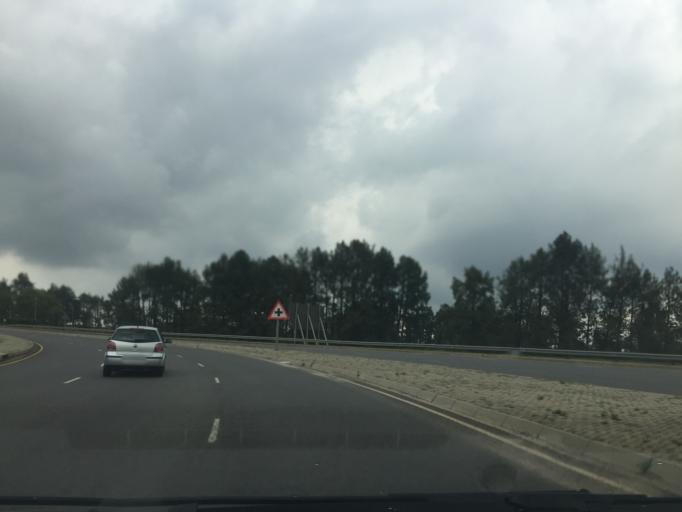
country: ZA
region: Gauteng
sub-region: City of Johannesburg Metropolitan Municipality
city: Modderfontein
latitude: -26.1092
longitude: 28.1495
